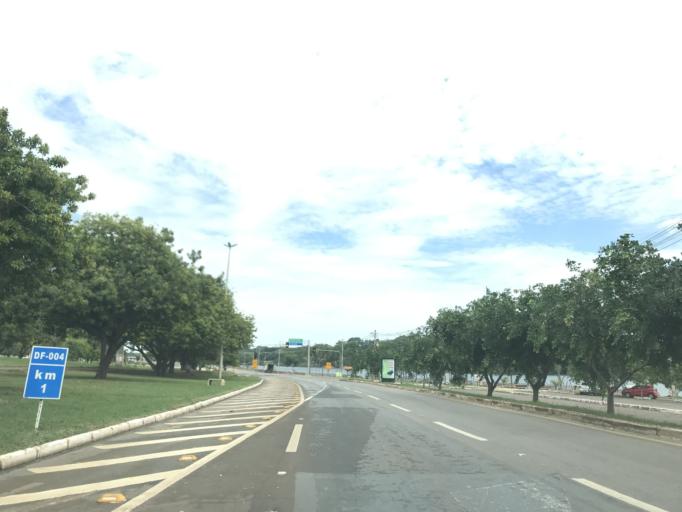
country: BR
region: Federal District
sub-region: Brasilia
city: Brasilia
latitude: -15.7345
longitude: -47.8853
